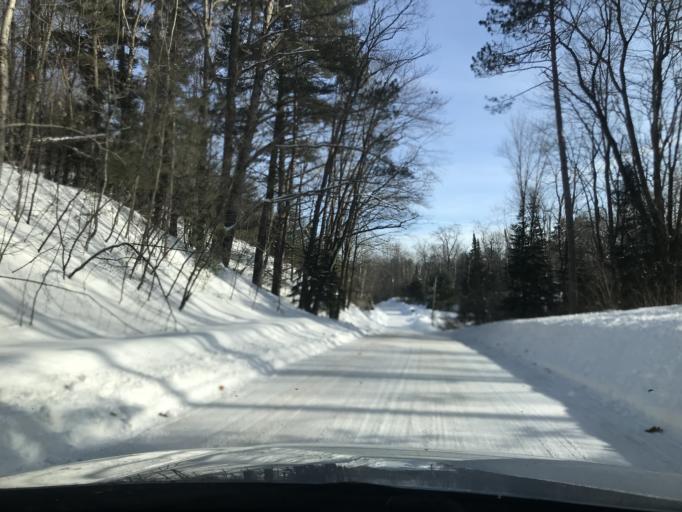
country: US
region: Wisconsin
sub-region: Menominee County
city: Legend Lake
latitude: 45.3436
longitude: -88.4552
